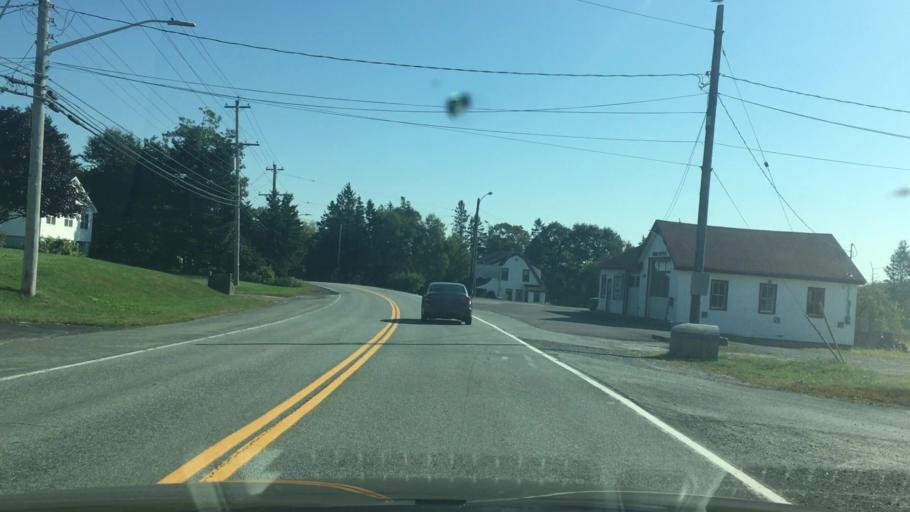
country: CA
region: Nova Scotia
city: Cole Harbour
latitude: 44.7833
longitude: -63.1537
